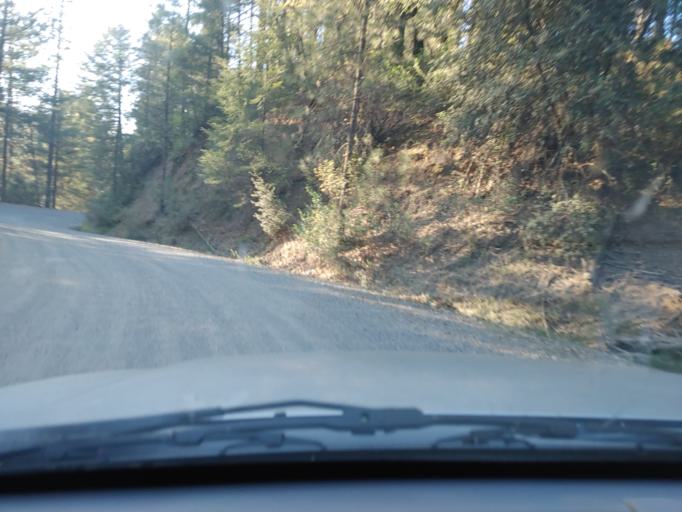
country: US
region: California
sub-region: Shasta County
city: Bella Vista
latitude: 40.8233
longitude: -122.0174
